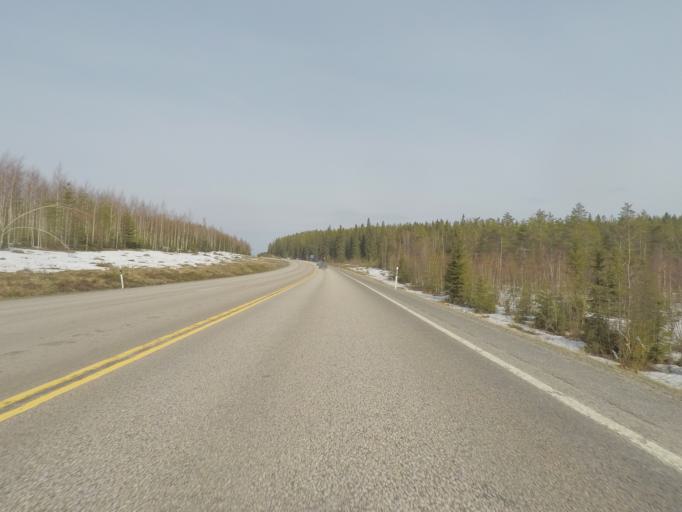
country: FI
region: Central Finland
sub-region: Jyvaeskylae
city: Toivakka
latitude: 62.0406
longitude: 26.0504
